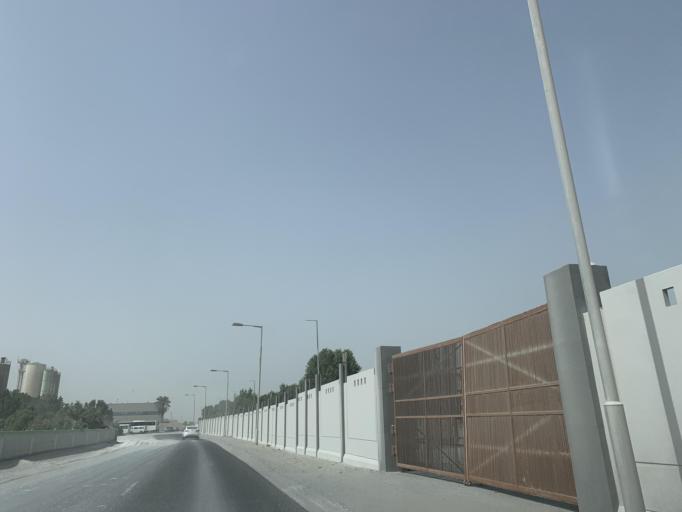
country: BH
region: Northern
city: Madinat `Isa
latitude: 26.1845
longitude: 50.5174
